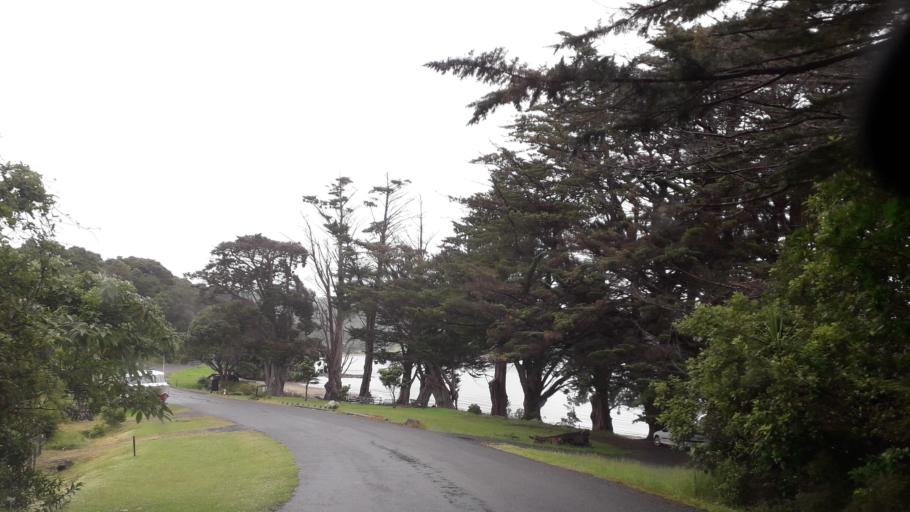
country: NZ
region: Northland
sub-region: Far North District
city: Paihia
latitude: -35.2314
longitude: 174.2608
